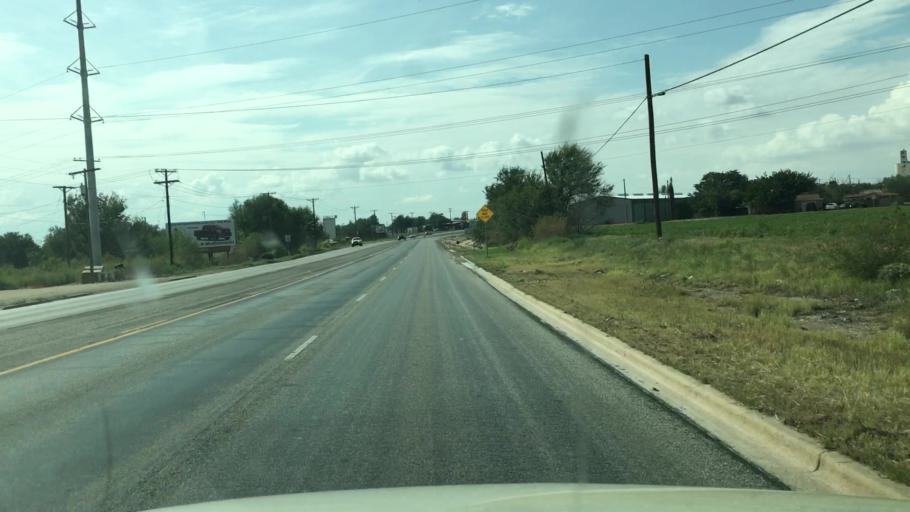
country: US
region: Texas
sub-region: Dawson County
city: Lamesa
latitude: 32.7177
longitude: -101.9420
